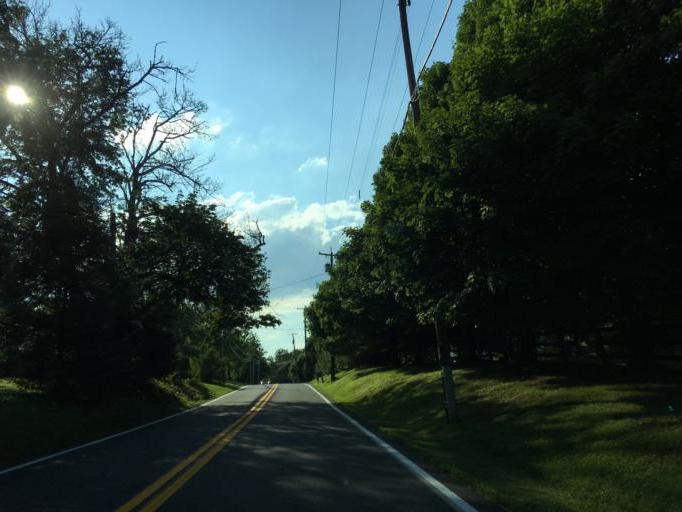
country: US
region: Maryland
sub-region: Baltimore County
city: Kingsville
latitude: 39.4691
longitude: -76.4433
